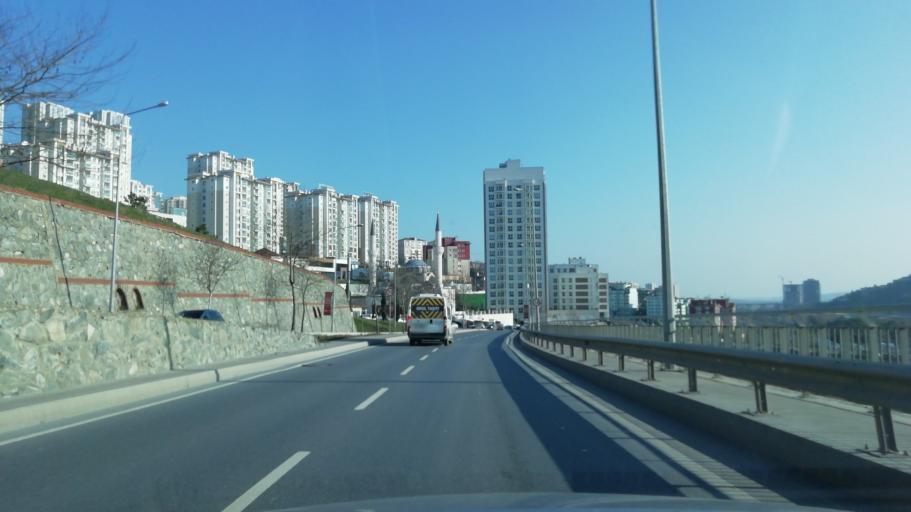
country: TR
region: Istanbul
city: Esenyurt
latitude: 41.0759
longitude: 28.6900
